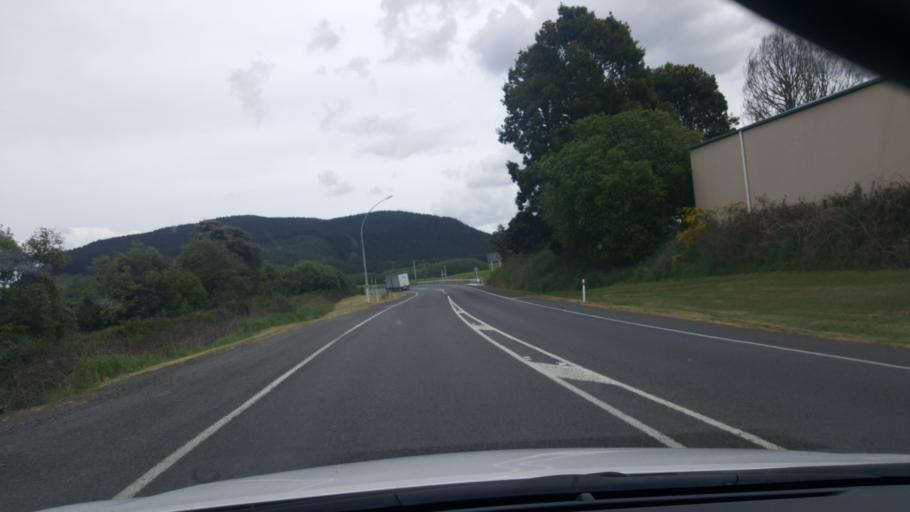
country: NZ
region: Bay of Plenty
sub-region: Rotorua District
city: Rotorua
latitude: -38.3417
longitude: 176.3630
